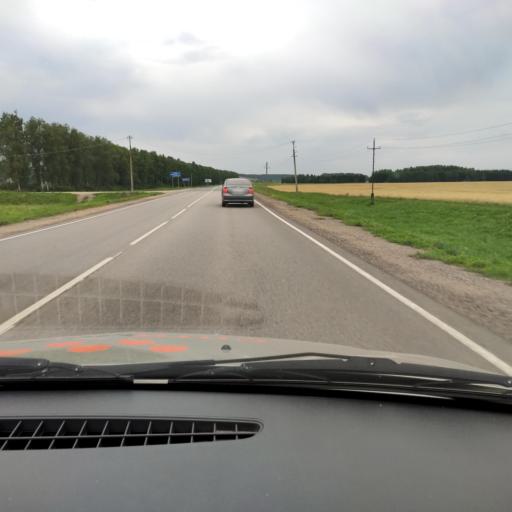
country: RU
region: Bashkortostan
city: Iglino
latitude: 54.9792
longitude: 56.5032
